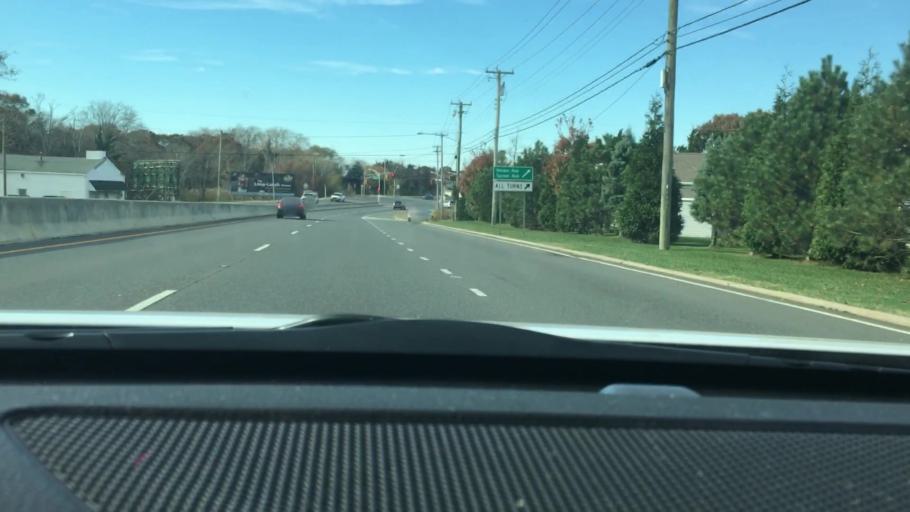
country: US
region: New Jersey
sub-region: Atlantic County
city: Absecon
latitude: 39.4190
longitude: -74.4950
